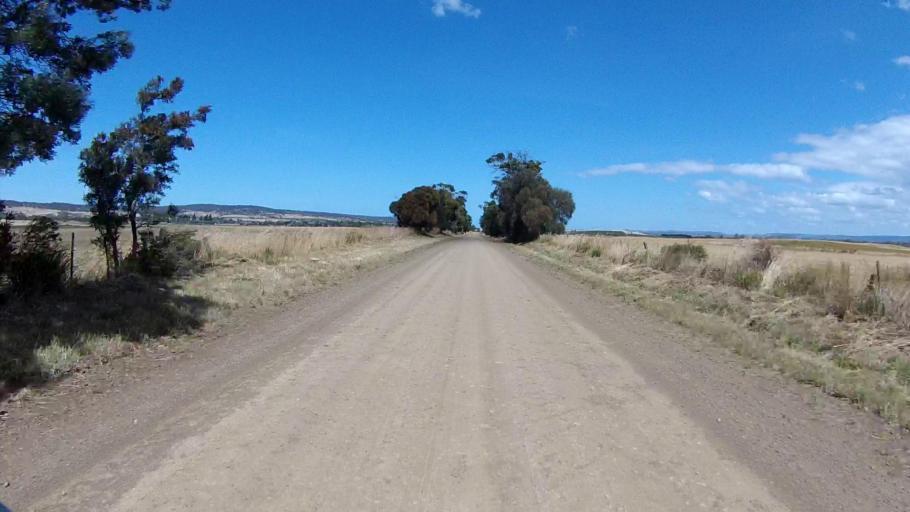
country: AU
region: Tasmania
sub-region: Break O'Day
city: St Helens
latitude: -41.9890
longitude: 148.0666
